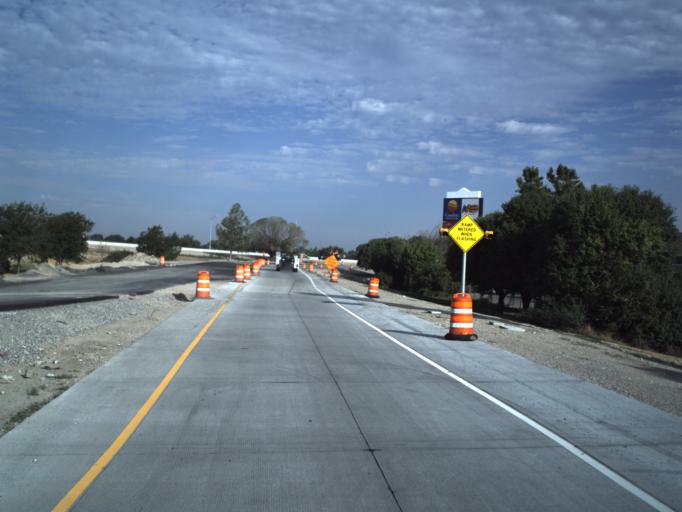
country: US
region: Utah
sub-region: Salt Lake County
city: Taylorsville
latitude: 40.6981
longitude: -111.9500
